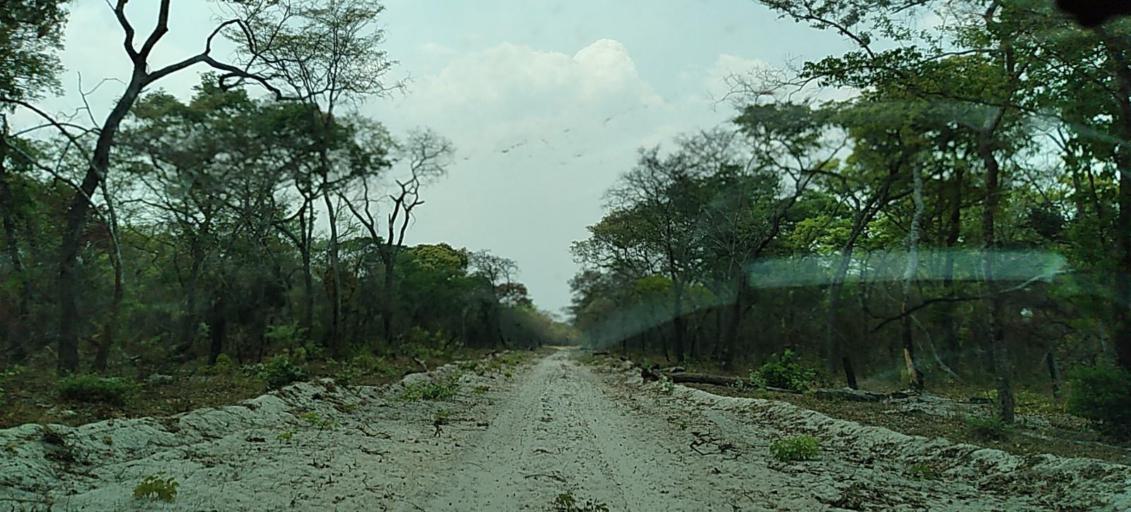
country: ZM
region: Western
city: Lukulu
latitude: -14.0087
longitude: 23.5829
